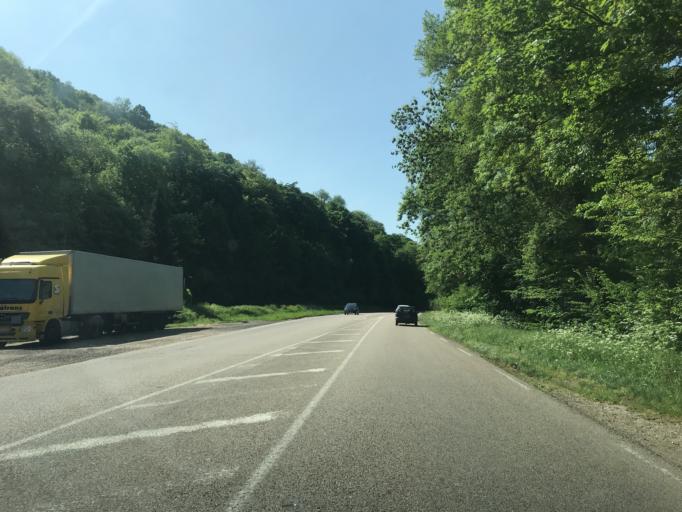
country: FR
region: Haute-Normandie
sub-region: Departement de la Seine-Maritime
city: Les Authieux-sur-le-Port-Saint-Ouen
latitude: 49.3491
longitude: 1.1275
